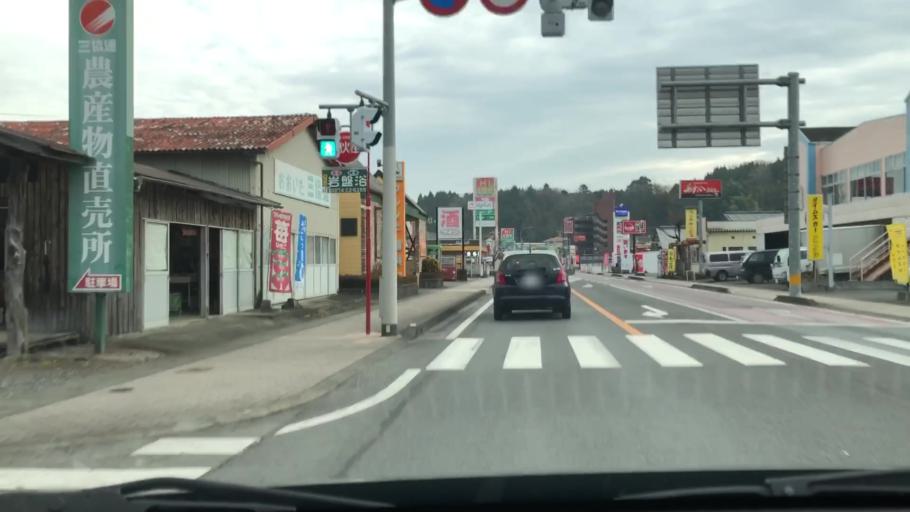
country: JP
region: Oita
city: Takedamachi
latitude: 32.9842
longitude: 131.5956
